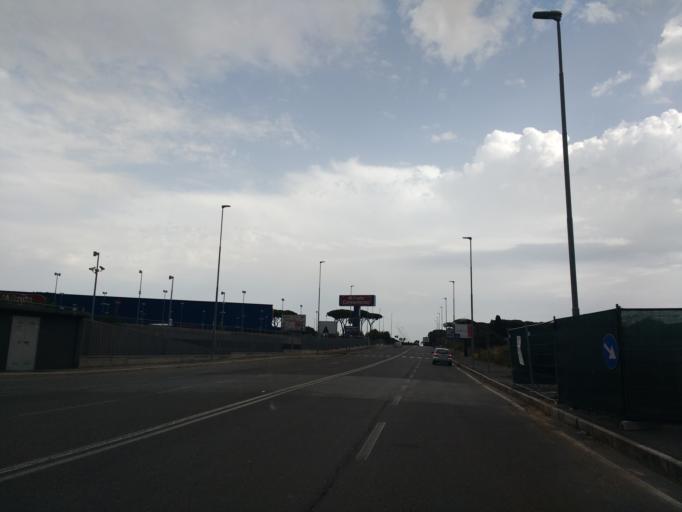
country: IT
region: Latium
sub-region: Citta metropolitana di Roma Capitale
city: Monte Migliore-La Selvotta
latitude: 41.7136
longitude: 12.4442
